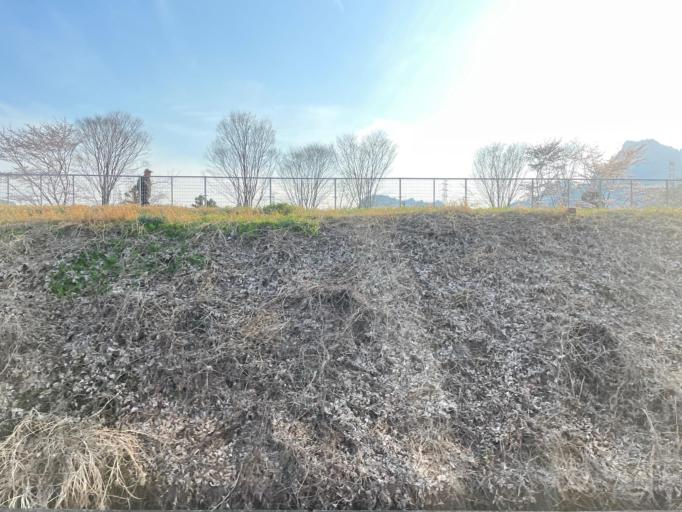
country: JP
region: Gunma
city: Annaka
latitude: 36.3135
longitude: 138.7908
